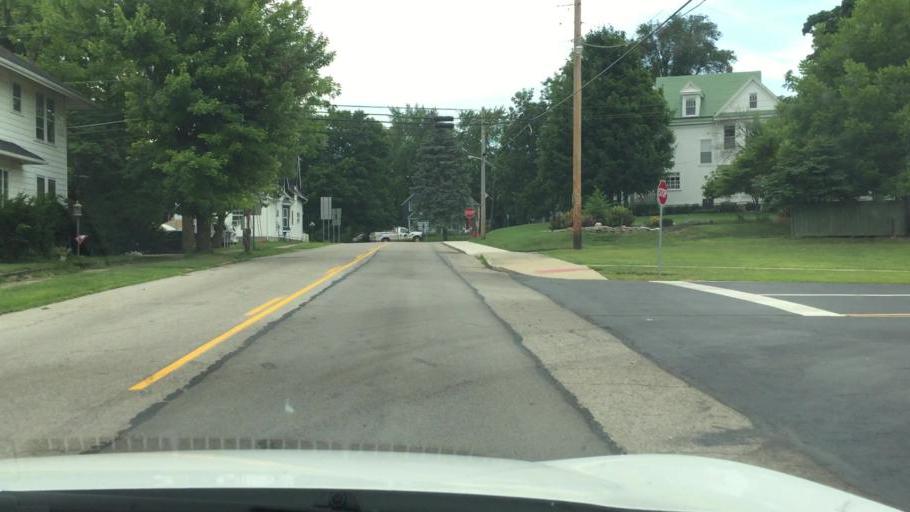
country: US
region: Ohio
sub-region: Champaign County
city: Mechanicsburg
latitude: 40.0746
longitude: -83.5585
